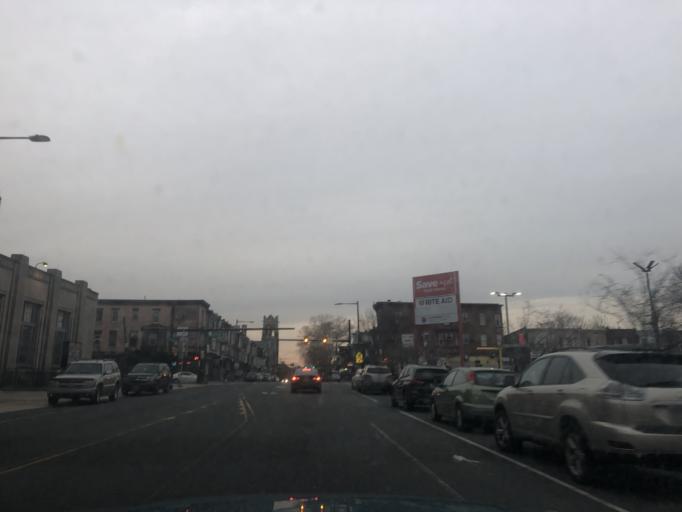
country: US
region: Pennsylvania
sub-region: Philadelphia County
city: Philadelphia
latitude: 39.9955
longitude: -75.1666
